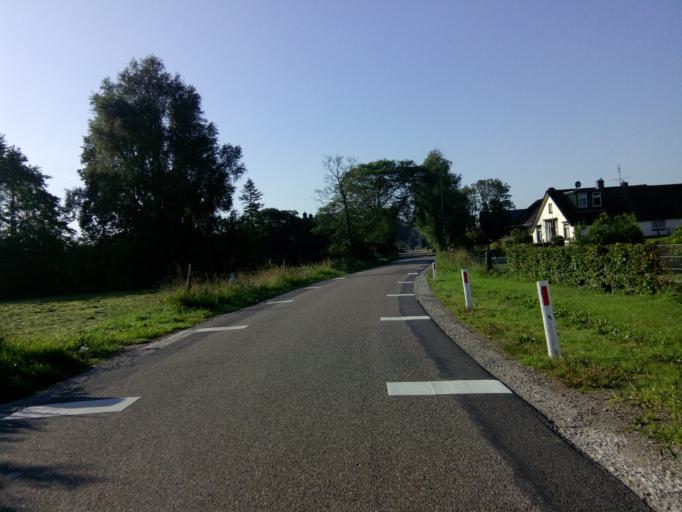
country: NL
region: Utrecht
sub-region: Gemeente Woudenberg
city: Woudenberg
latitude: 52.0766
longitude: 5.4494
